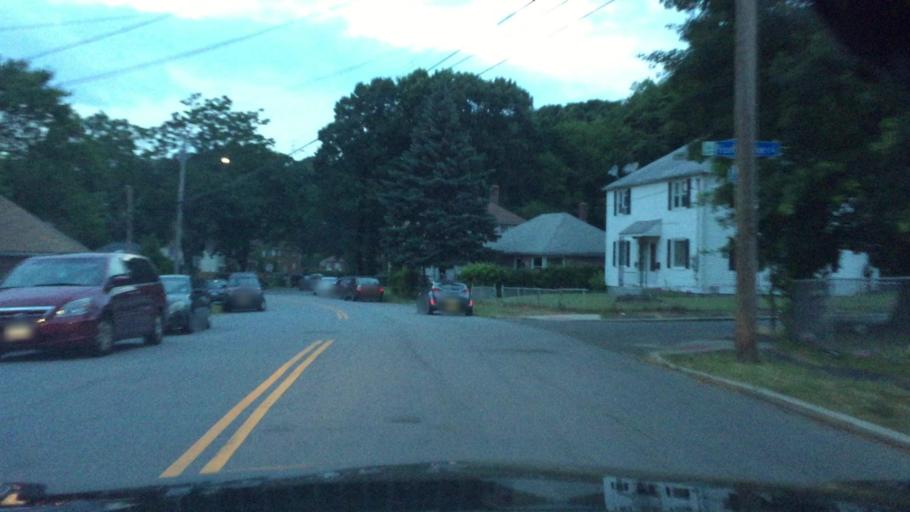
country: US
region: Connecticut
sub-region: Fairfield County
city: Stratford
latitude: 41.2039
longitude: -73.1585
